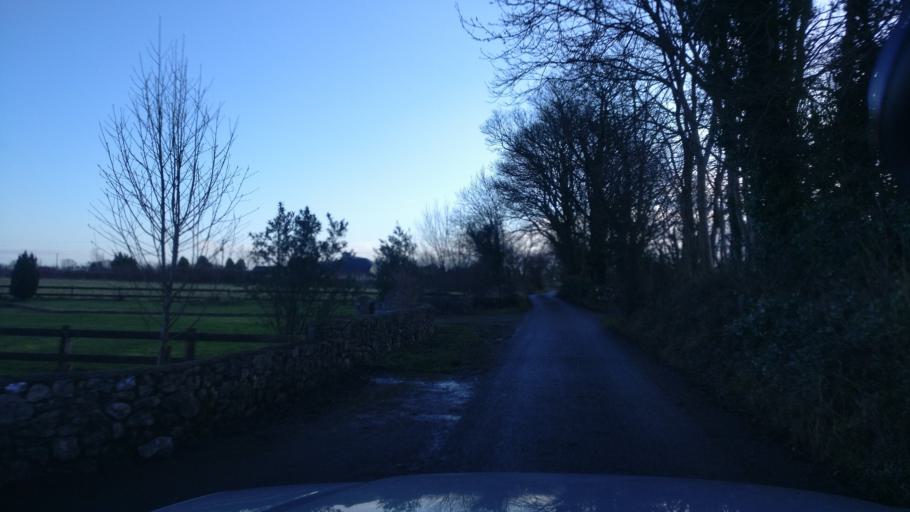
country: IE
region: Connaught
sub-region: County Galway
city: Loughrea
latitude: 53.2369
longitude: -8.5767
